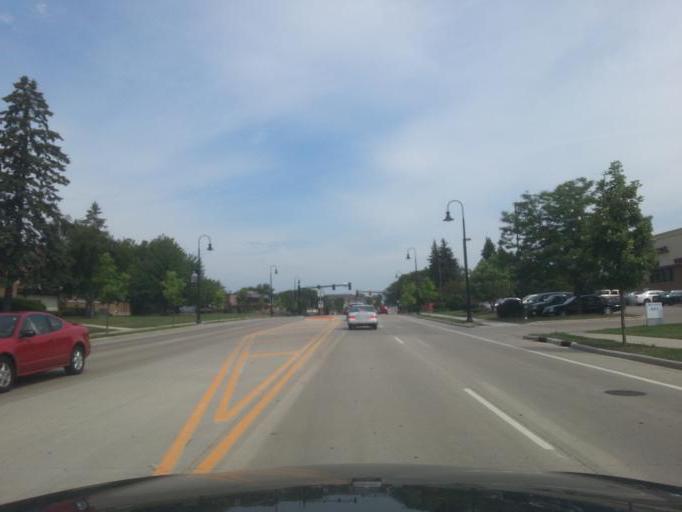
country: US
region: Wisconsin
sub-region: Dane County
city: Monona
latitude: 43.0610
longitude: -89.3260
